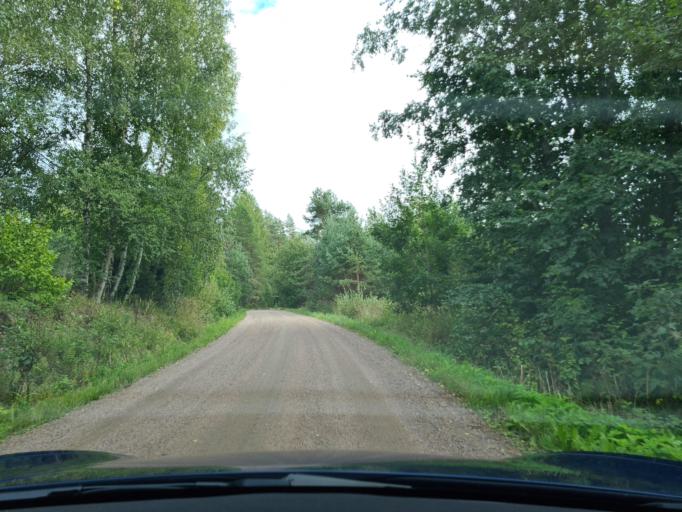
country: FI
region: Uusimaa
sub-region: Helsinki
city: Vihti
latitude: 60.4227
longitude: 24.4751
